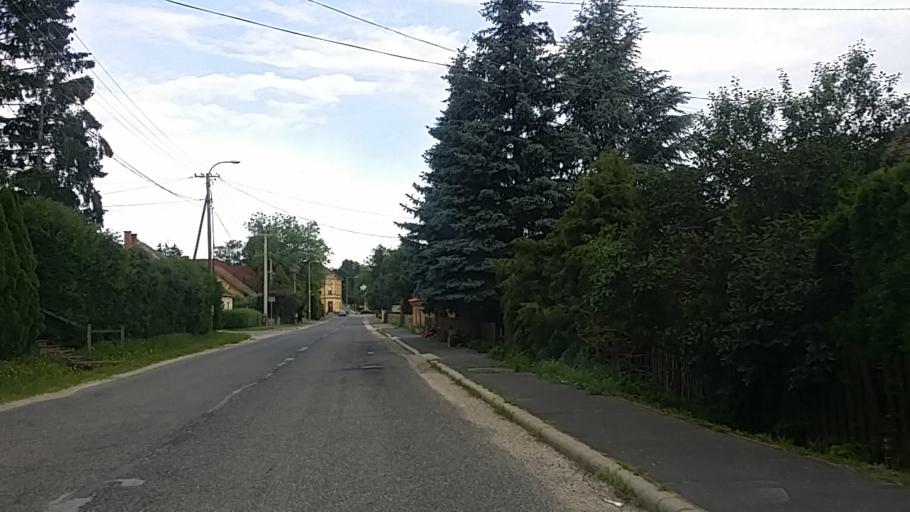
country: SI
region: Hodos-Hodos
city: Hodos
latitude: 46.8375
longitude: 16.4232
